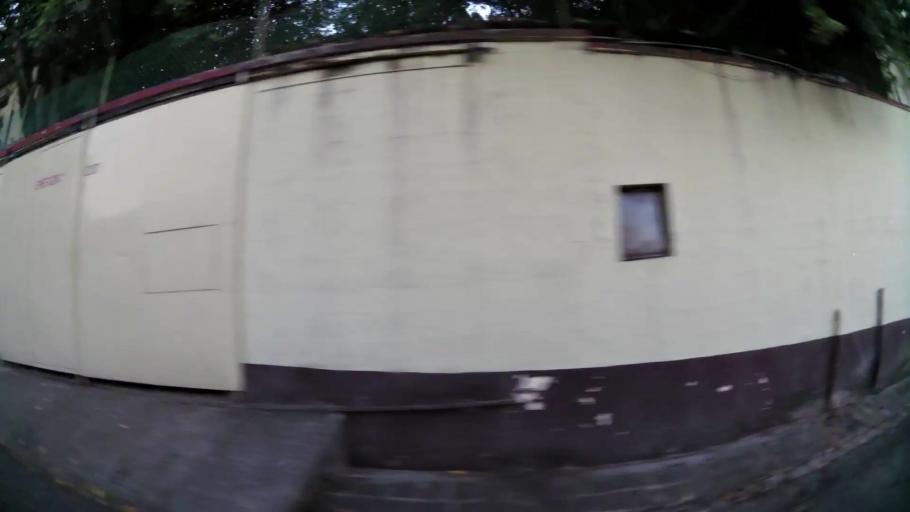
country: MU
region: Port Louis
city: Port Louis
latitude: -20.1679
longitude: 57.5119
